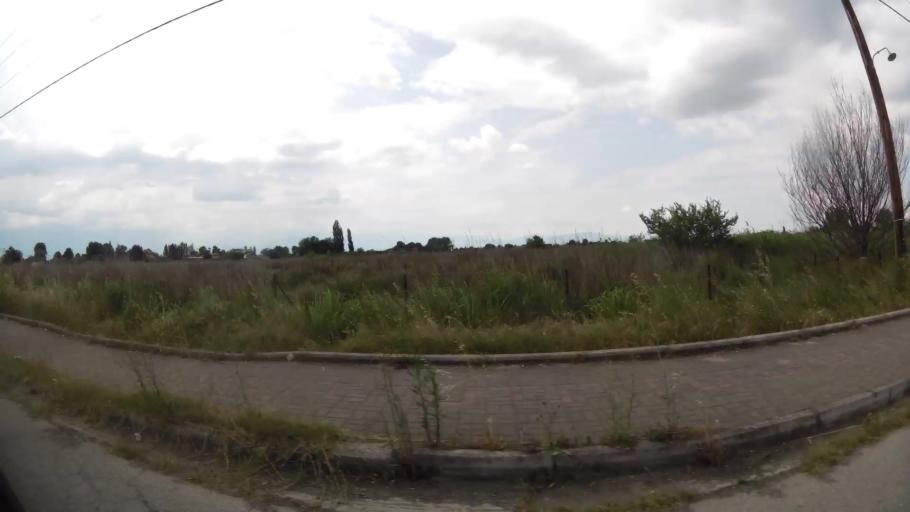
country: GR
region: Central Macedonia
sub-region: Nomos Pierias
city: Paralia
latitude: 40.2708
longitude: 22.5944
